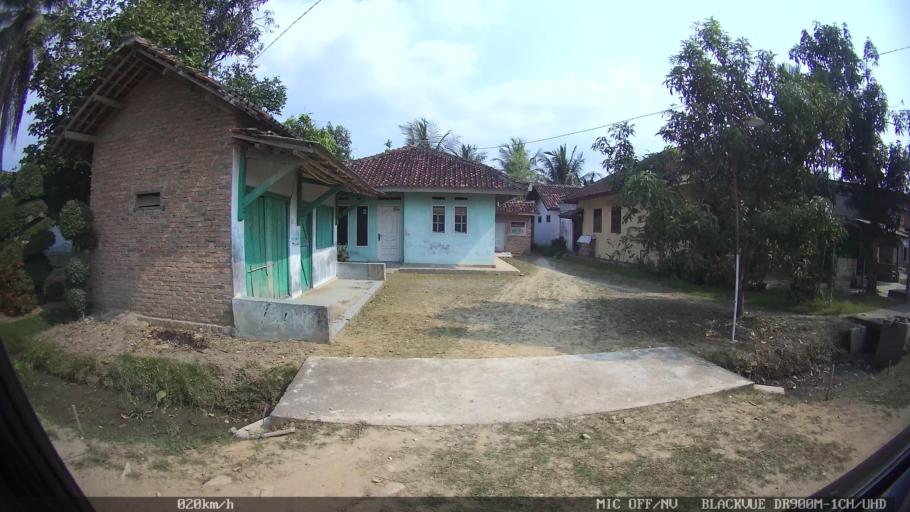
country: ID
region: Lampung
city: Kedondong
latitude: -5.4099
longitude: 104.9990
